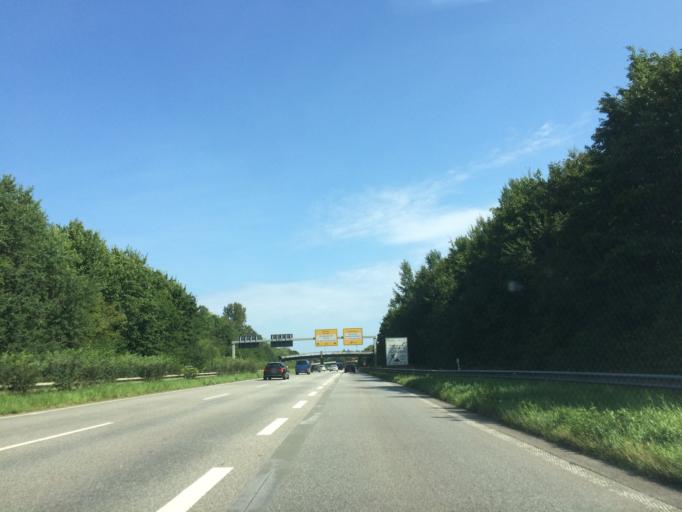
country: DE
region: Schleswig-Holstein
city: Kiel
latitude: 54.3411
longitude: 10.1156
